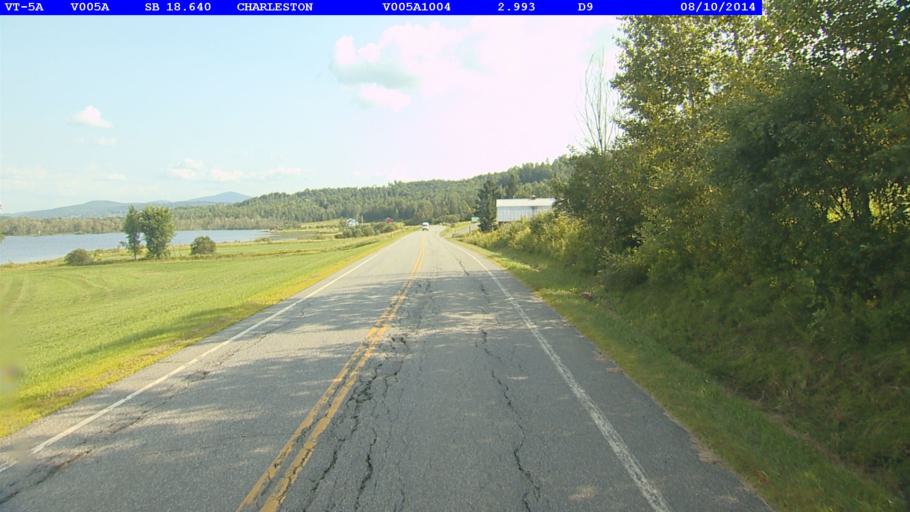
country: US
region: Vermont
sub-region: Orleans County
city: Newport
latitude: 44.8735
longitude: -72.0610
